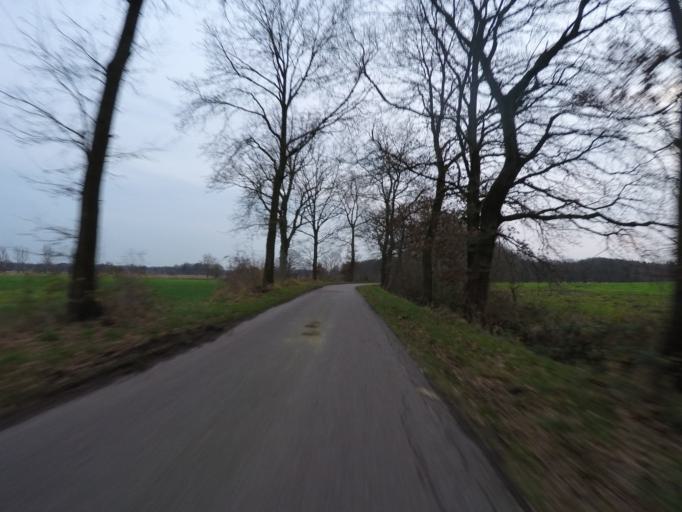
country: DE
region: Schleswig-Holstein
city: Bilsen
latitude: 53.7363
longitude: 9.8694
